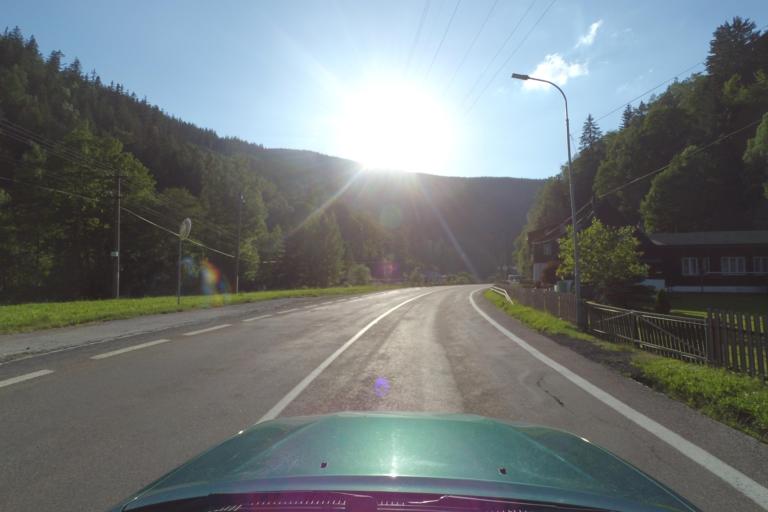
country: CZ
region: Kralovehradecky
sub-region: Okres Trutnov
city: Svoboda nad Upou
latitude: 50.6646
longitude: 15.7996
